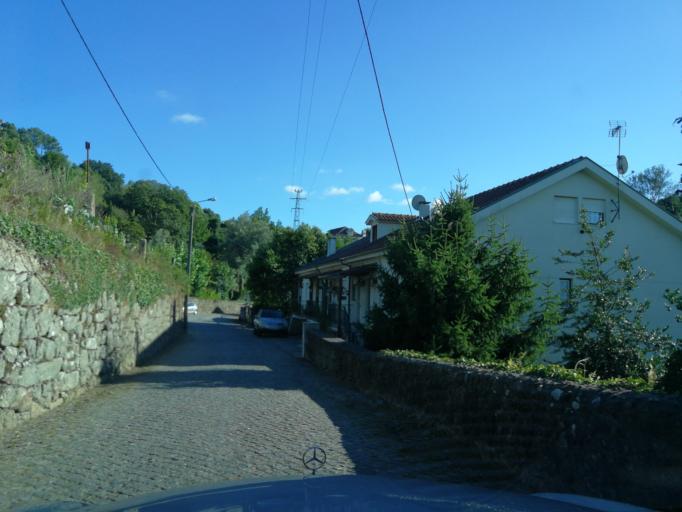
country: PT
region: Braga
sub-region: Braga
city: Adaufe
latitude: 41.5576
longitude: -8.3872
